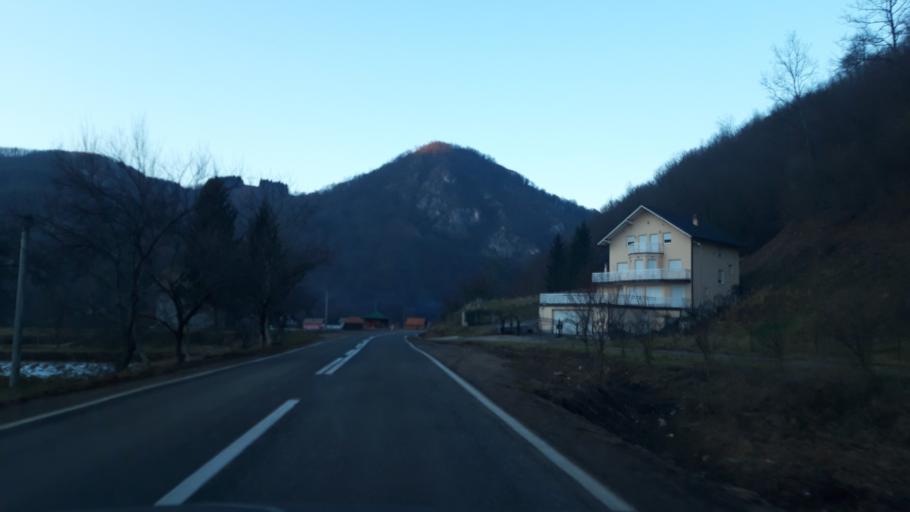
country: BA
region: Republika Srpska
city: Milici
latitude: 44.2613
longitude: 19.1048
